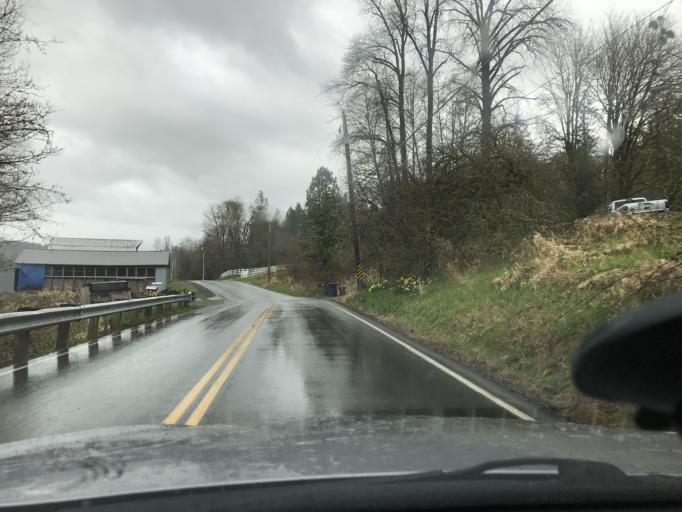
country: US
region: Washington
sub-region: King County
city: Ames Lake
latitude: 47.6687
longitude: -121.9747
